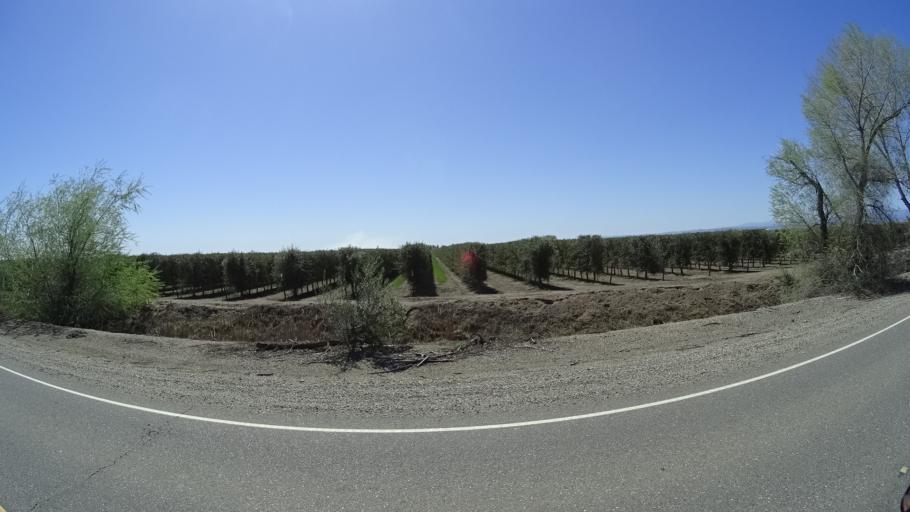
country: US
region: California
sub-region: Glenn County
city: Willows
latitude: 39.6246
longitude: -122.2393
